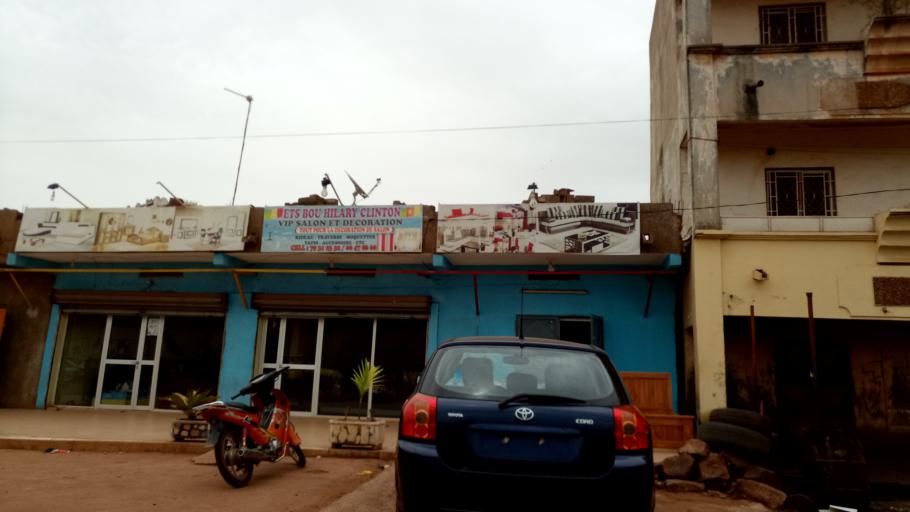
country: ML
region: Bamako
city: Bamako
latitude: 12.5896
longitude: -7.9869
